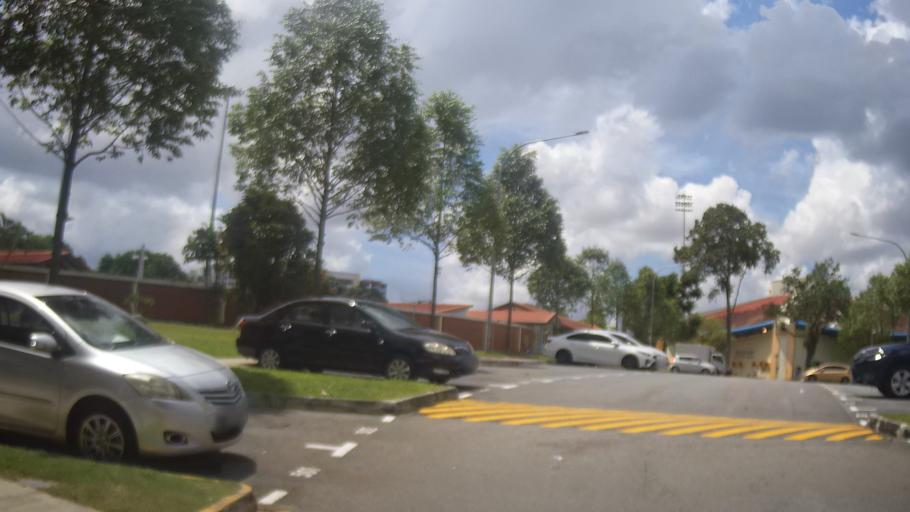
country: MY
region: Johor
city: Johor Bahru
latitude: 1.4342
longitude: 103.7784
